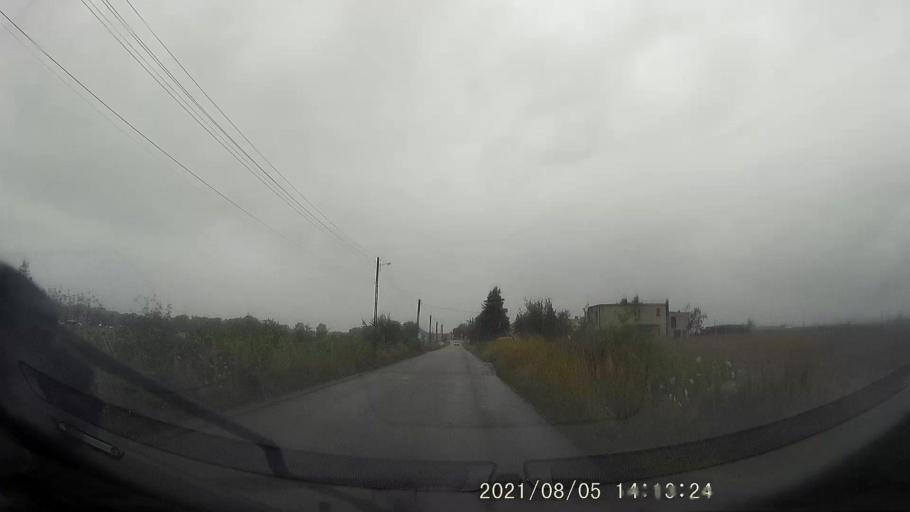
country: PL
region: Opole Voivodeship
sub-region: Powiat krapkowicki
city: Strzeleczki
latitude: 50.4702
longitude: 17.7478
